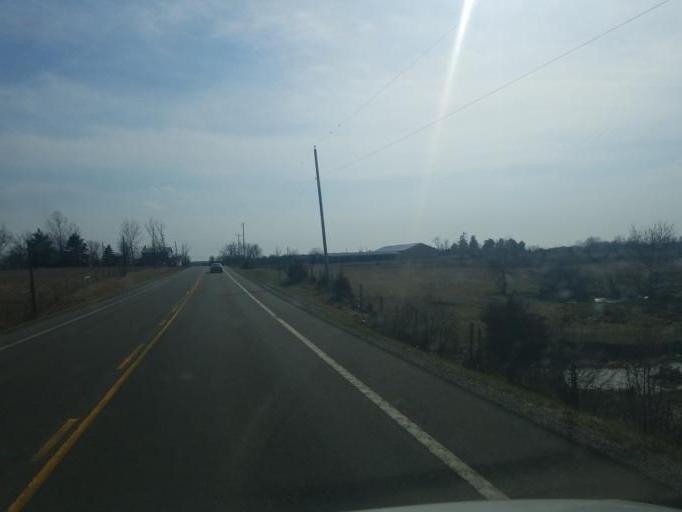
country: US
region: Ohio
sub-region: Logan County
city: Northwood
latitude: 40.4573
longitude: -83.7227
